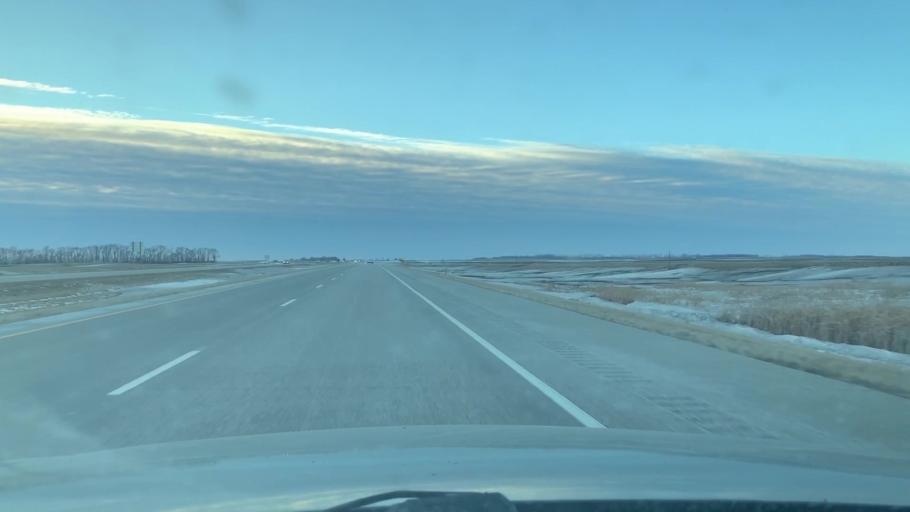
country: US
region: North Dakota
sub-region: Cass County
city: Casselton
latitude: 46.8758
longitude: -97.4946
